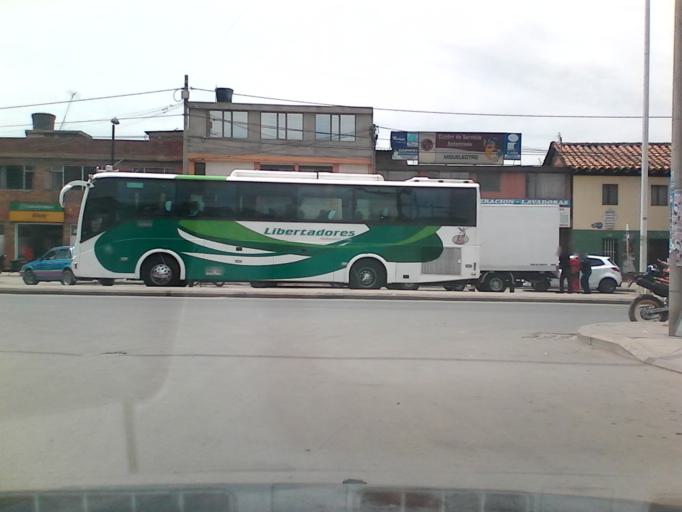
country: CO
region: Boyaca
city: Sogamoso
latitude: 5.7185
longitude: -72.9349
